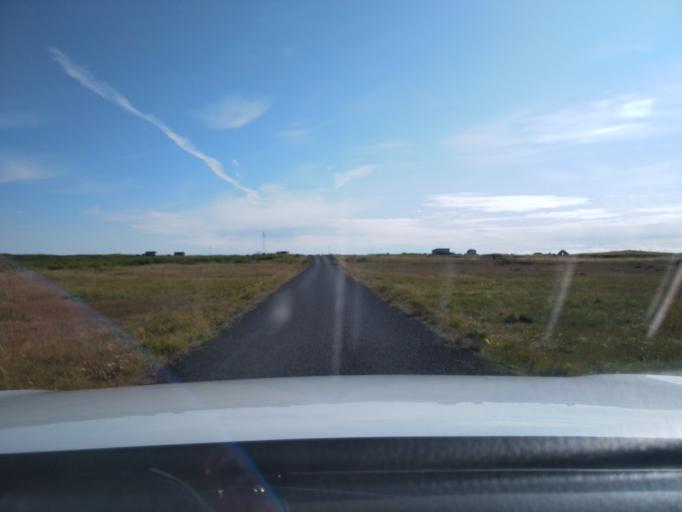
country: IS
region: South
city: THorlakshoefn
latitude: 63.8333
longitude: -21.6958
